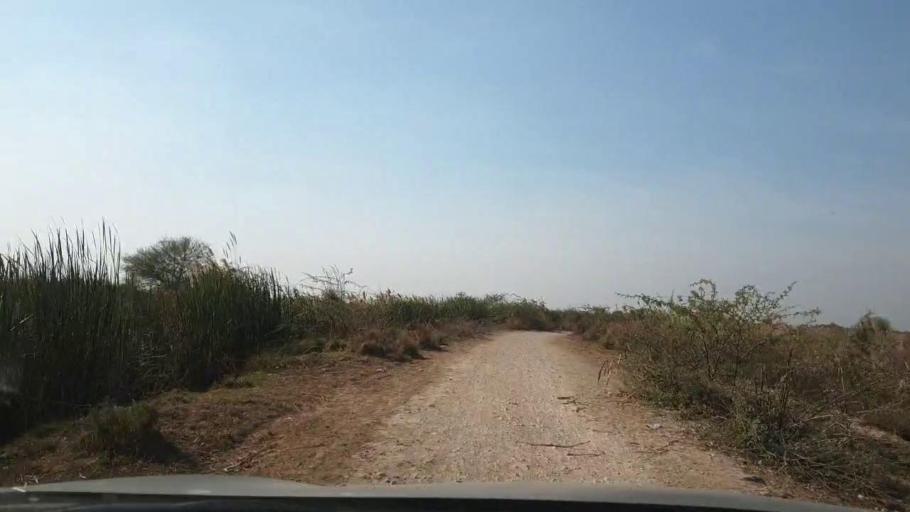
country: PK
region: Sindh
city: Berani
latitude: 25.7180
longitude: 68.7707
